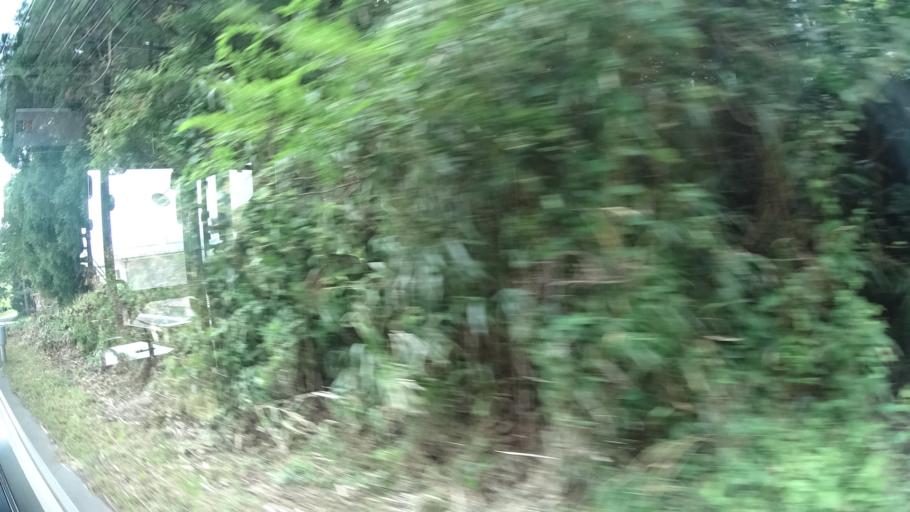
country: JP
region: Miyagi
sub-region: Oshika Gun
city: Onagawa Cho
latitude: 38.6676
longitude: 141.4437
